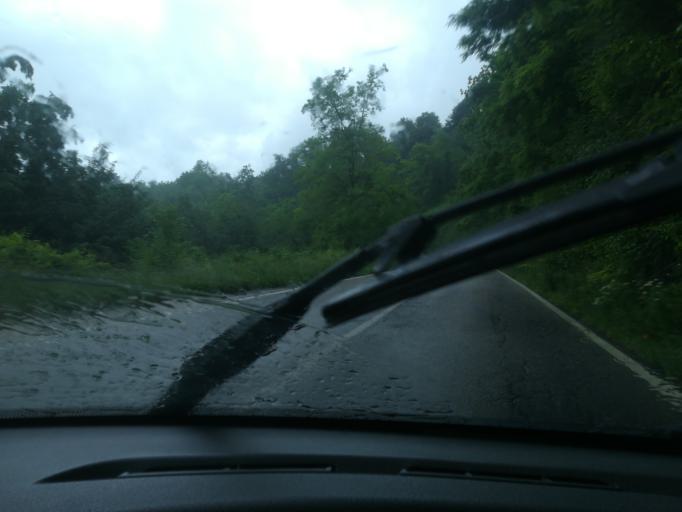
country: IT
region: The Marches
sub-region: Province of Fermo
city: Amandola
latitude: 43.0000
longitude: 13.3315
